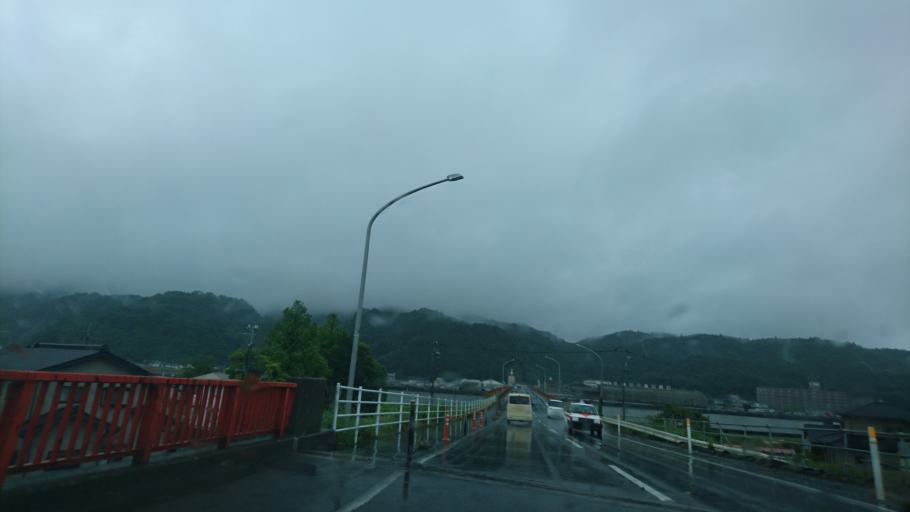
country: JP
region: Miyagi
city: Ishinomaki
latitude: 38.4397
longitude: 141.3145
